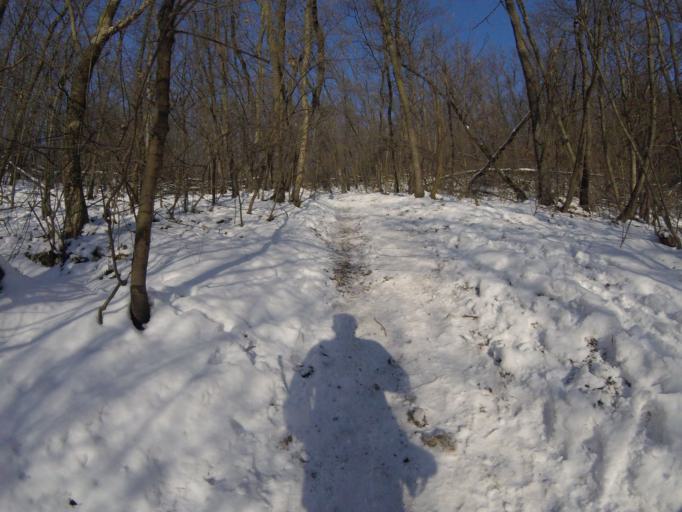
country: HU
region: Pest
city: Piliscsaba
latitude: 47.6445
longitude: 18.8348
